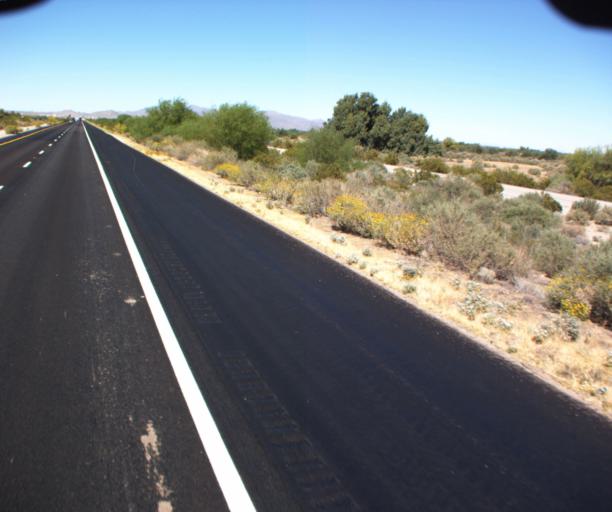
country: US
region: Arizona
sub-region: Maricopa County
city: Buckeye
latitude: 33.3237
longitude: -112.6230
